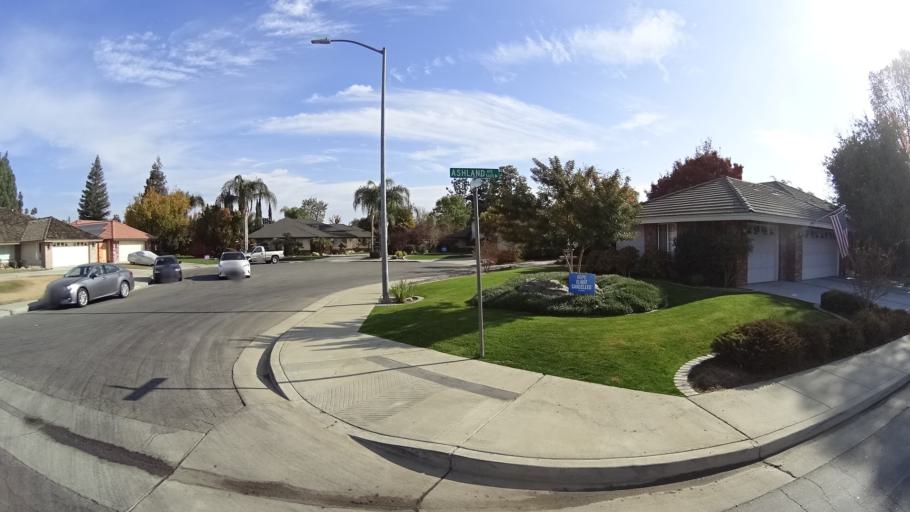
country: US
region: California
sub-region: Kern County
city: Greenacres
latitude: 35.4110
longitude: -119.0738
